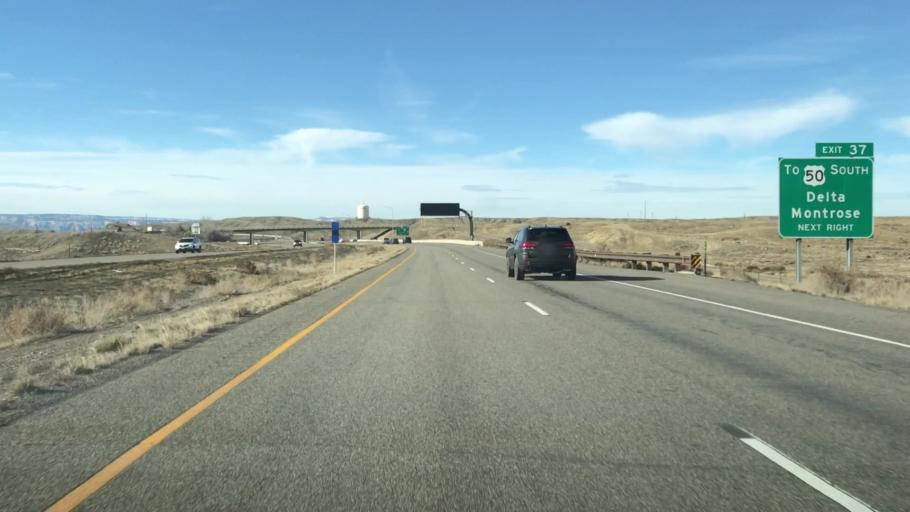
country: US
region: Colorado
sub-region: Mesa County
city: Clifton
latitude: 39.1075
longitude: -108.4368
